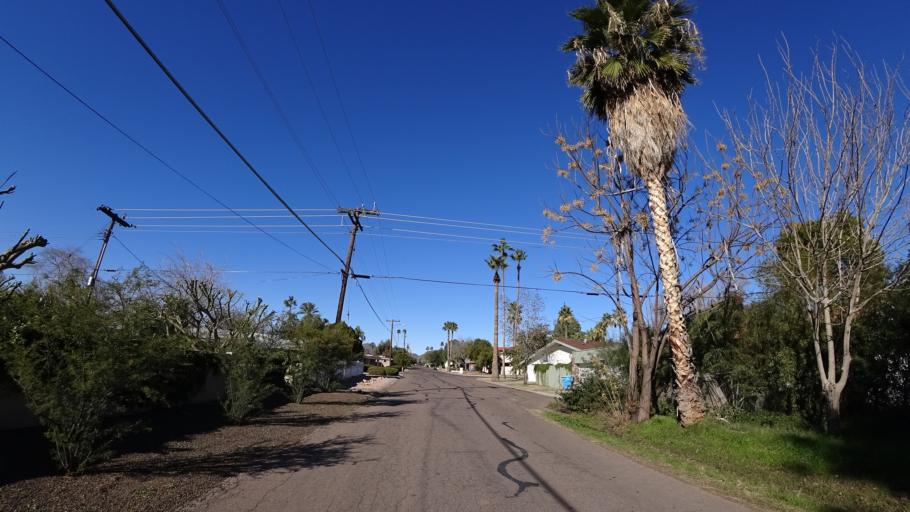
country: US
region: Arizona
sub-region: Maricopa County
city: Phoenix
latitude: 33.5446
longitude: -112.0783
